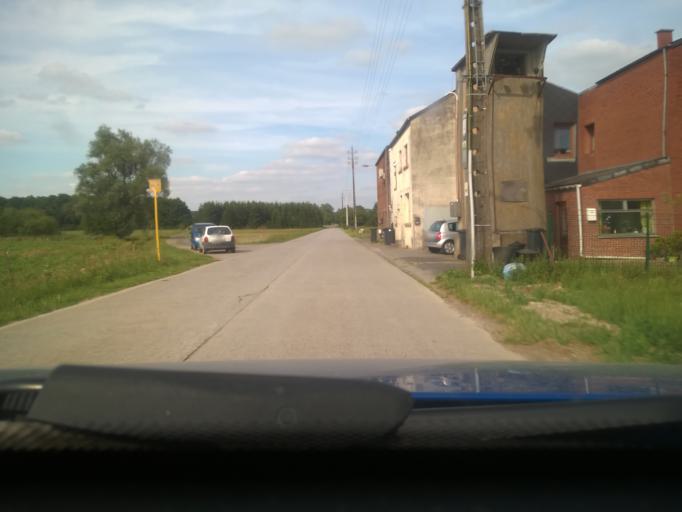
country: BE
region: Wallonia
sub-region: Province de Namur
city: Couvin
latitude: 50.1030
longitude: 4.5452
